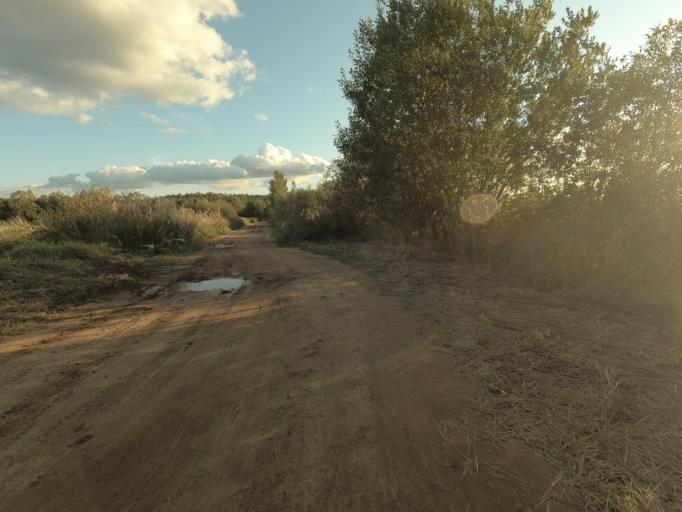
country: RU
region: Leningrad
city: Otradnoye
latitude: 59.8568
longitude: 30.7967
